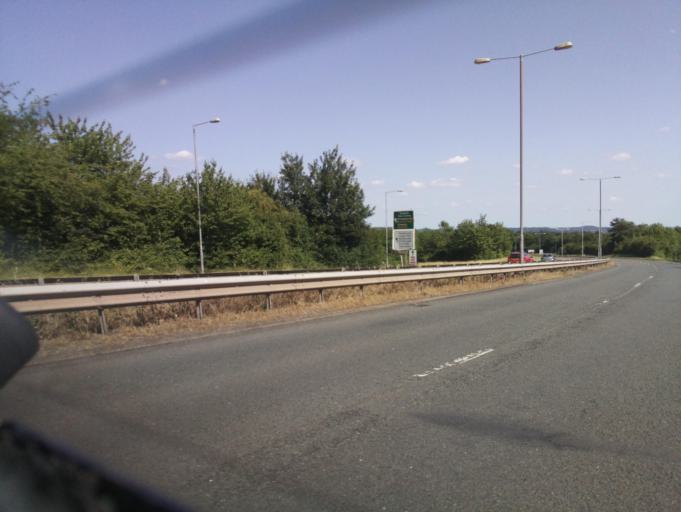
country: GB
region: England
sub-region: Worcestershire
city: Redditch
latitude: 52.2918
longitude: -1.9406
